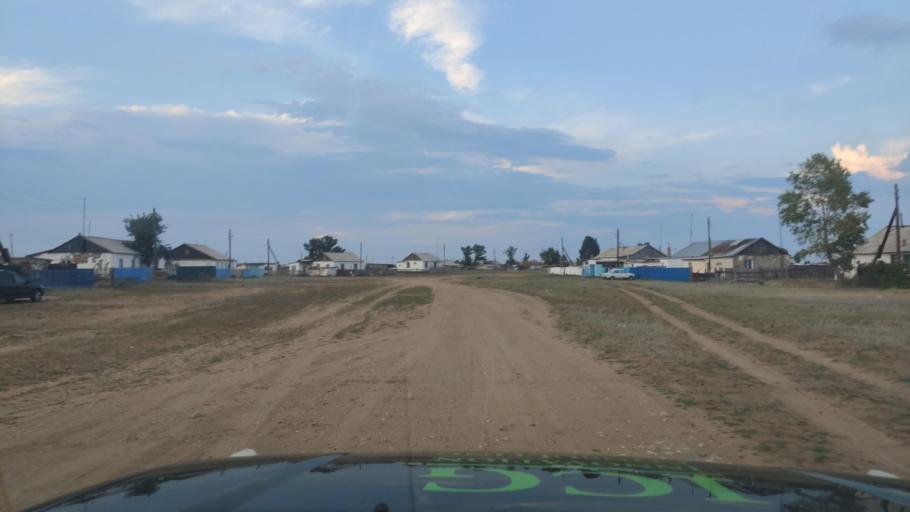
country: KZ
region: Pavlodar
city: Pavlodar
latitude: 52.2889
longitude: 77.4413
